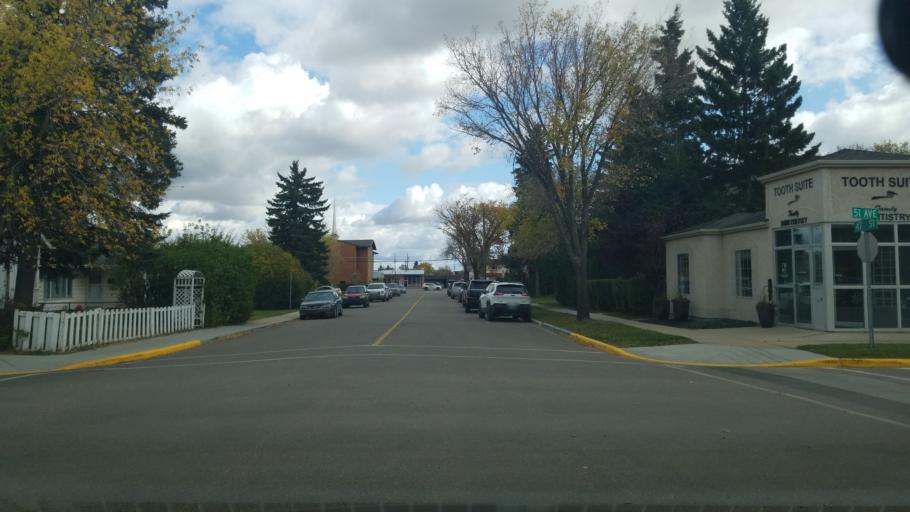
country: CA
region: Saskatchewan
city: Lloydminster
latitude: 53.2807
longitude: -110.0081
